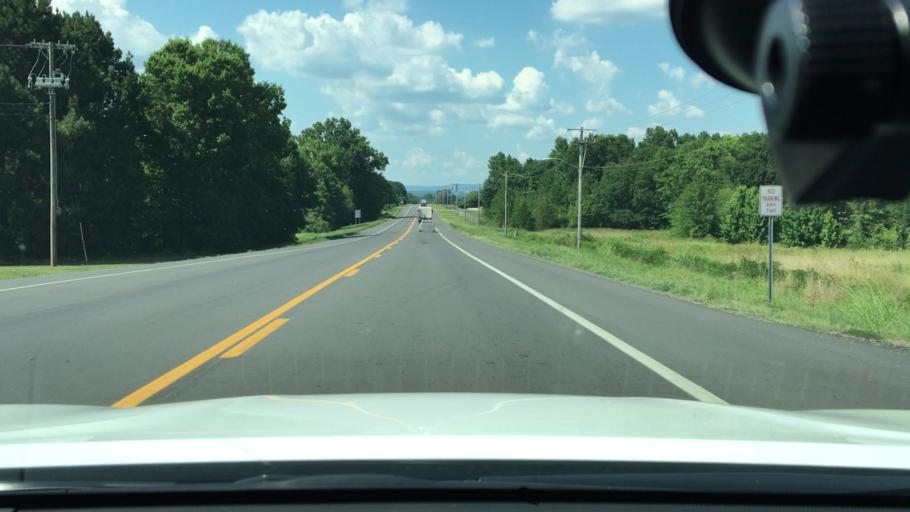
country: US
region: Arkansas
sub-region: Johnson County
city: Clarksville
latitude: 35.4331
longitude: -93.5294
